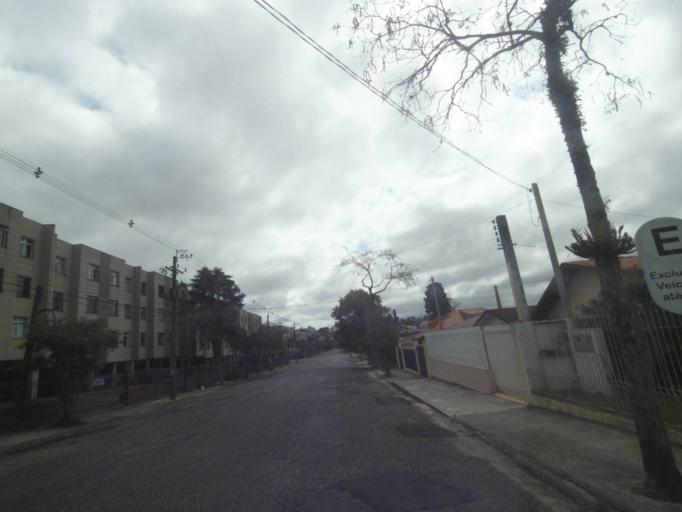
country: BR
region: Parana
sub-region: Curitiba
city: Curitiba
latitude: -25.3940
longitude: -49.2269
